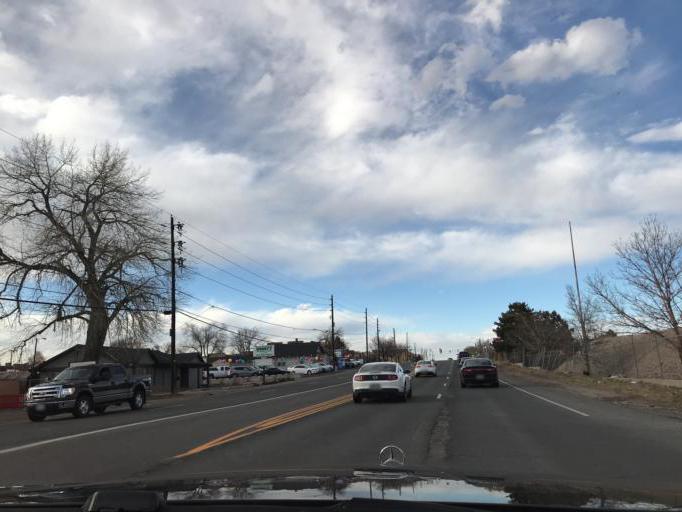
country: US
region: Colorado
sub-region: Jefferson County
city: Applewood
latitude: 39.7883
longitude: -105.1380
